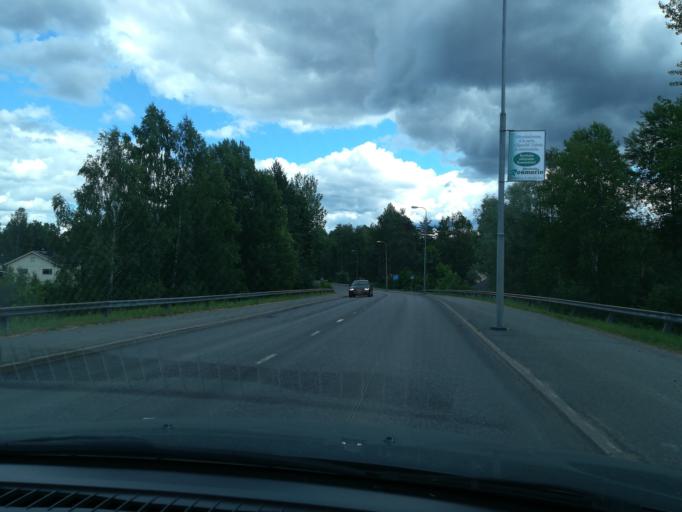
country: FI
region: Southern Savonia
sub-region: Mikkeli
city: Maentyharju
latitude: 61.4181
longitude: 26.8857
